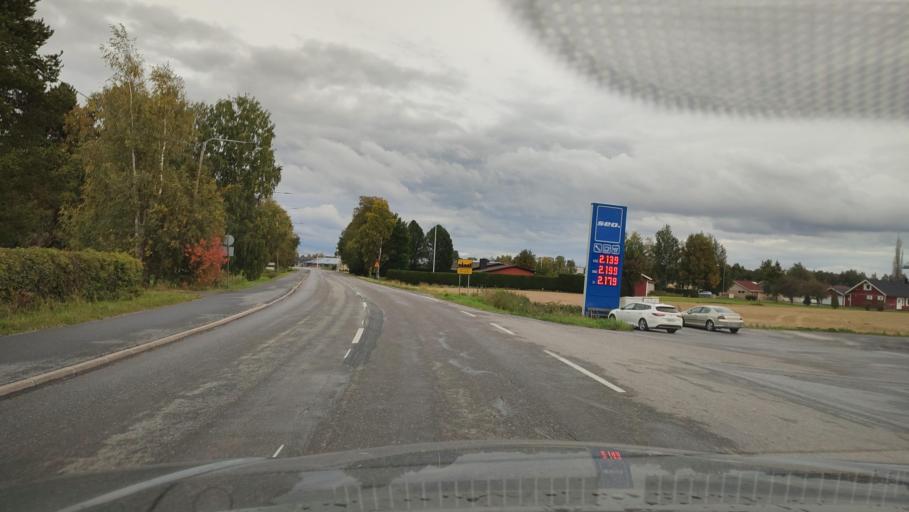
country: FI
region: Ostrobothnia
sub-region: Sydosterbotten
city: Kristinestad
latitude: 62.2550
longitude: 21.5019
